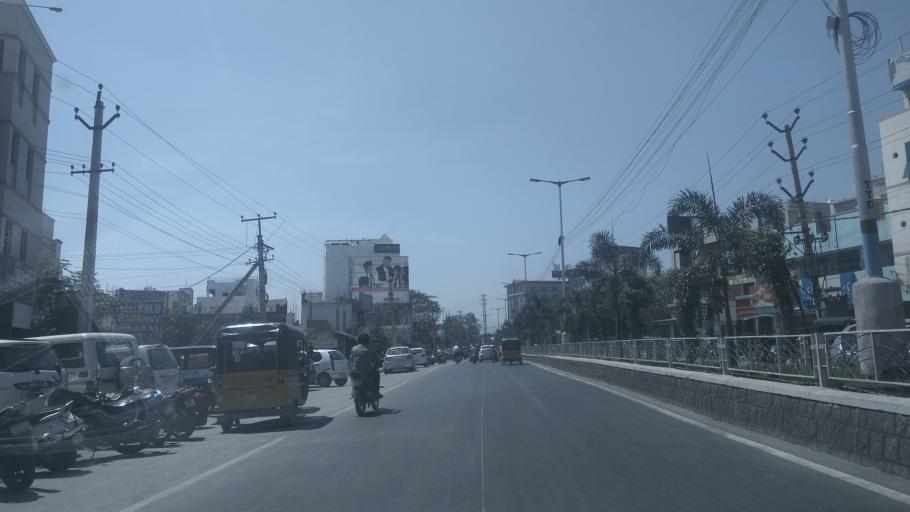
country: IN
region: Andhra Pradesh
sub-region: Chittoor
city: Tirupati
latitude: 13.6251
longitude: 79.4307
